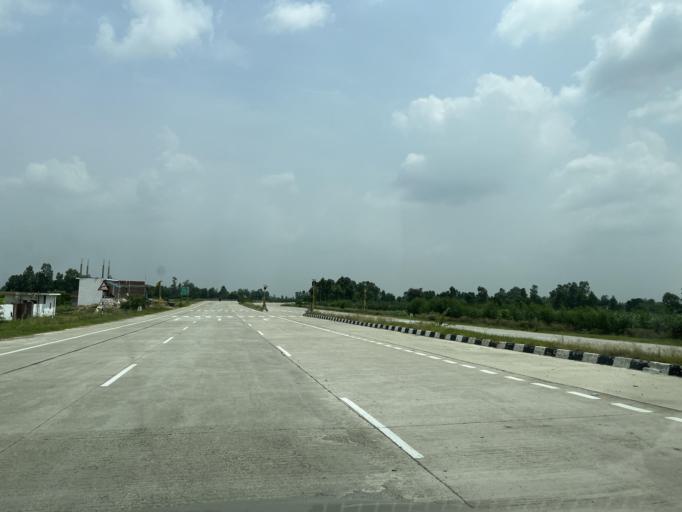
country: IN
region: Uttar Pradesh
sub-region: Bijnor
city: Nagina
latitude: 29.4310
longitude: 78.4101
